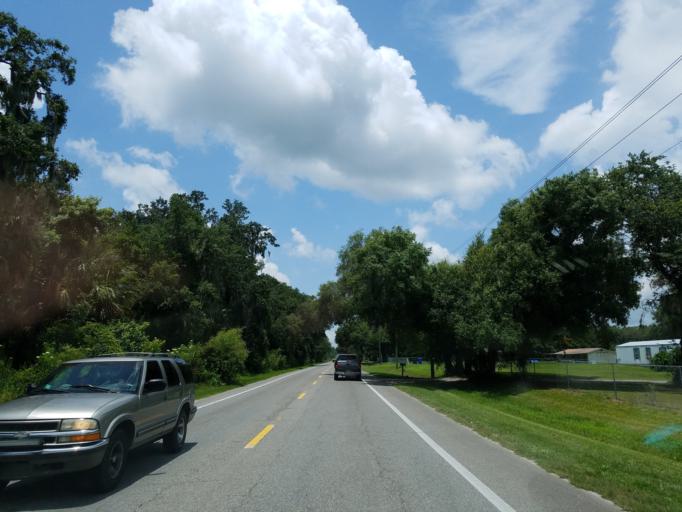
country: US
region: Florida
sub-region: Hillsborough County
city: Fish Hawk
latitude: 27.8506
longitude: -82.1094
